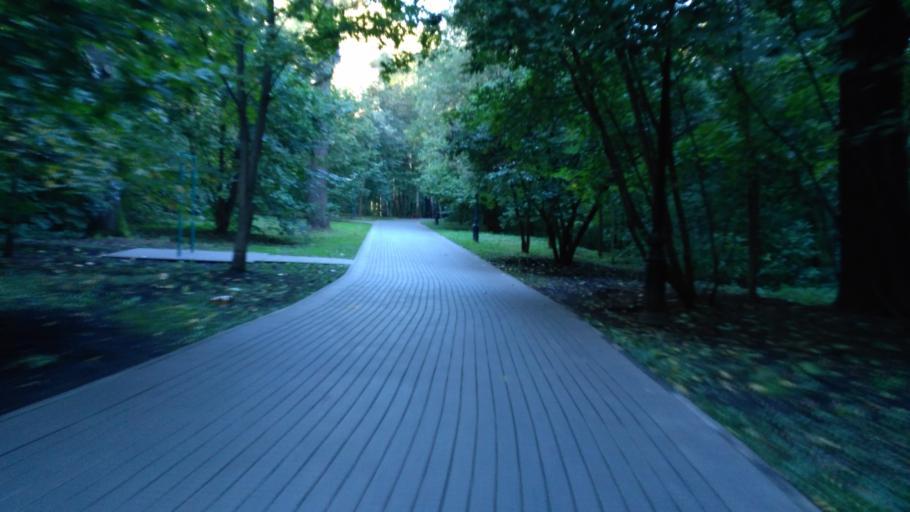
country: RU
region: Moscow
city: Ostankinskiy
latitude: 55.8288
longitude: 37.6057
